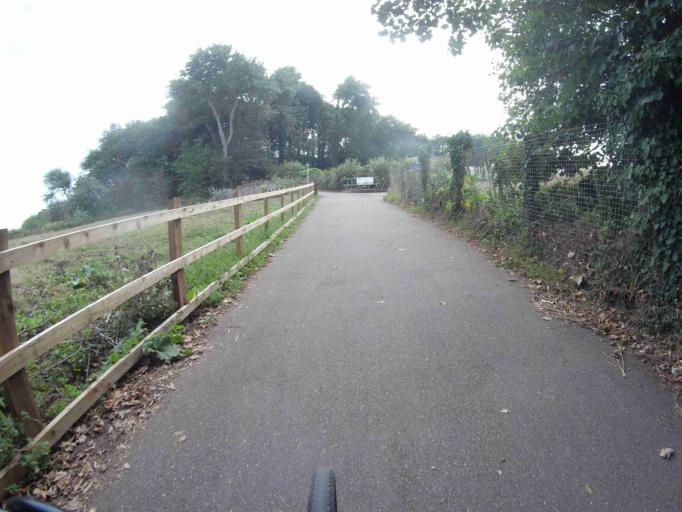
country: GB
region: England
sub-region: Devon
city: Dawlish
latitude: 50.5943
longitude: -3.4447
